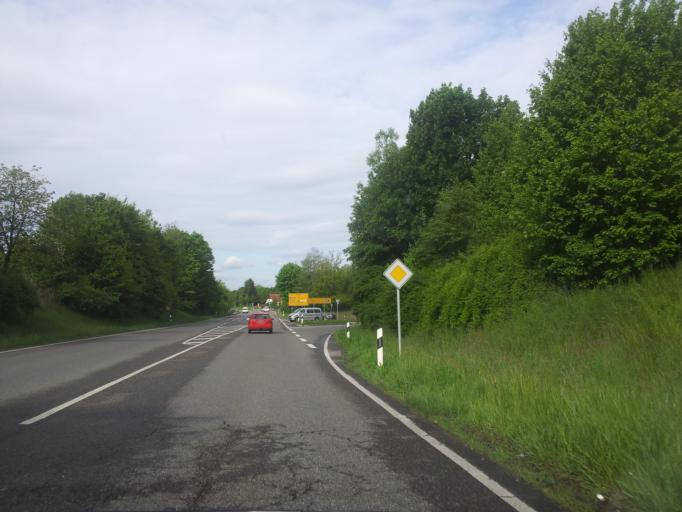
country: DE
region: Bavaria
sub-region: Swabia
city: Weissensberg
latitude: 47.5765
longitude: 9.7135
